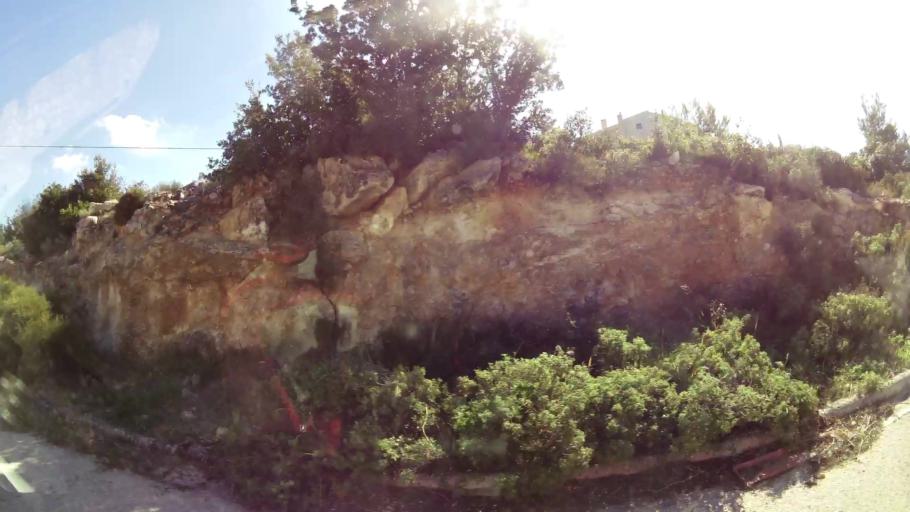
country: GR
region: Attica
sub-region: Nomarchia Anatolikis Attikis
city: Dhrafi
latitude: 38.0177
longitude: 23.9183
